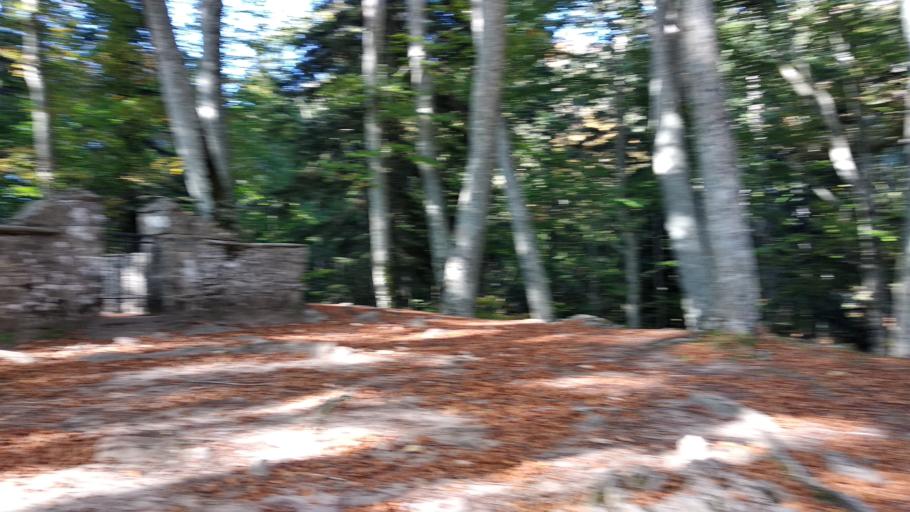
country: IT
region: Tuscany
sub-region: Province of Arezzo
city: Chiusi della Verna
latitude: 43.7079
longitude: 11.9302
